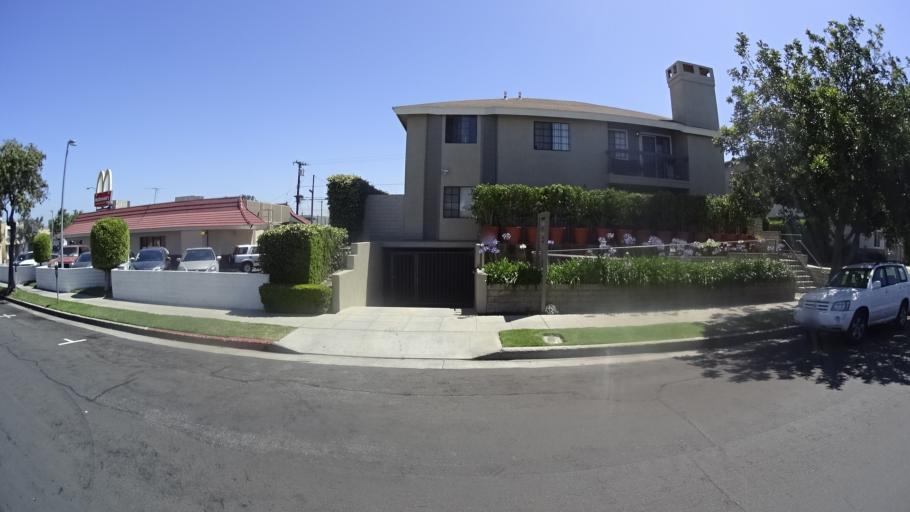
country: US
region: California
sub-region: Los Angeles County
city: Santa Monica
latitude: 34.0244
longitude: -118.4591
